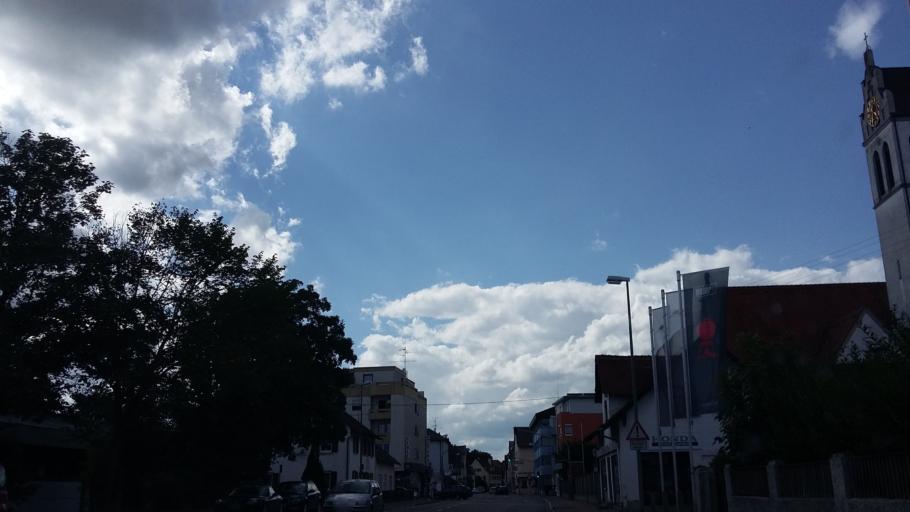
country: DE
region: Bavaria
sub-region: Swabia
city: Guenzburg
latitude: 48.4536
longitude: 10.2834
